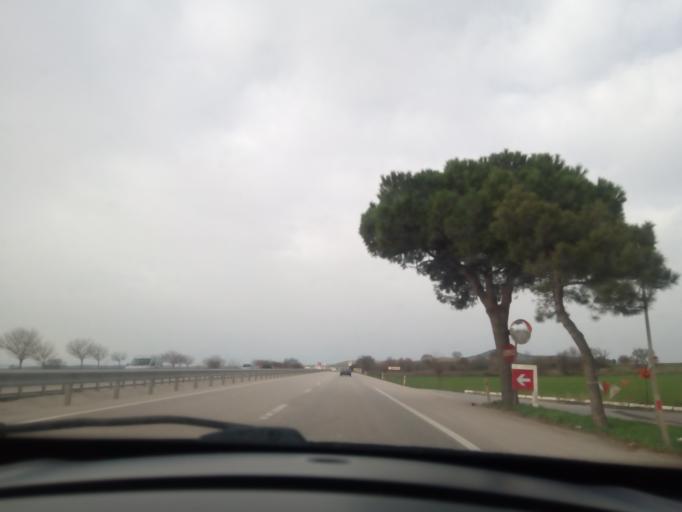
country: TR
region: Bursa
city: Gorukle
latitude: 40.2145
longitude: 28.7392
